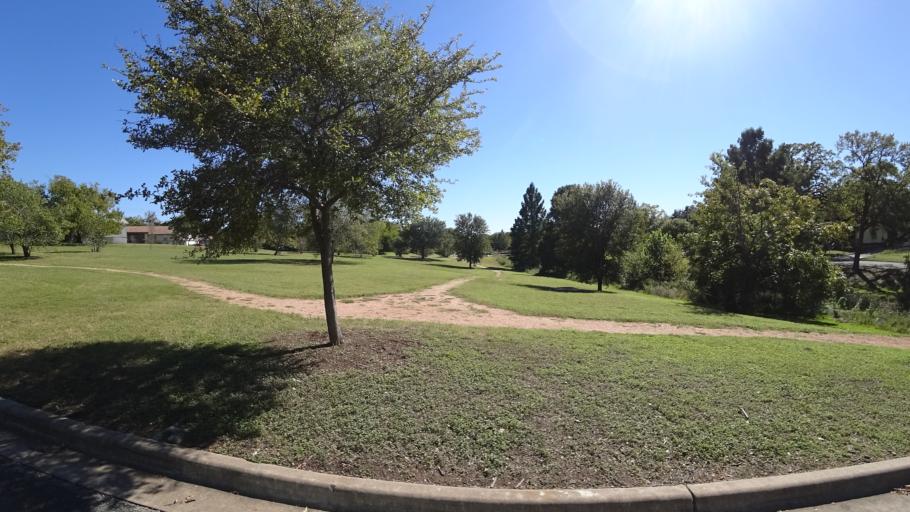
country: US
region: Texas
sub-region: Travis County
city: Austin
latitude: 30.2859
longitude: -97.7008
